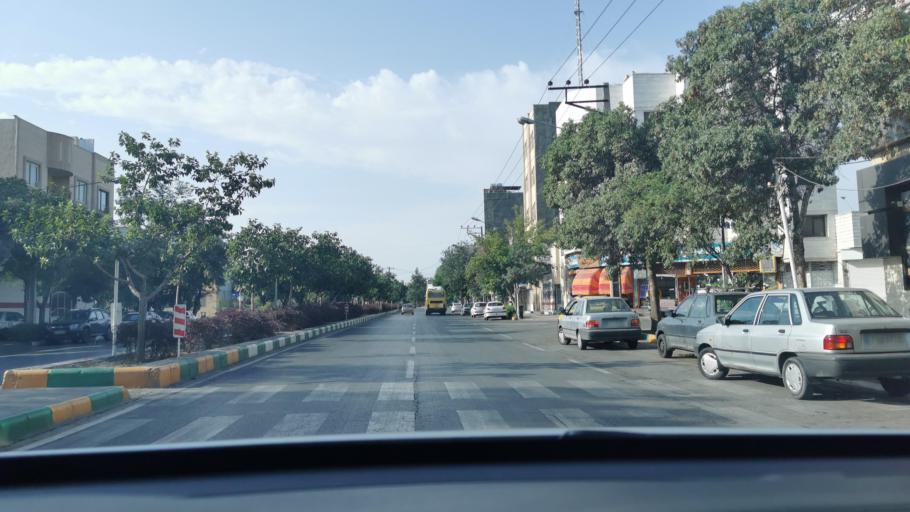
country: IR
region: Razavi Khorasan
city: Mashhad
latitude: 36.2663
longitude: 59.6196
